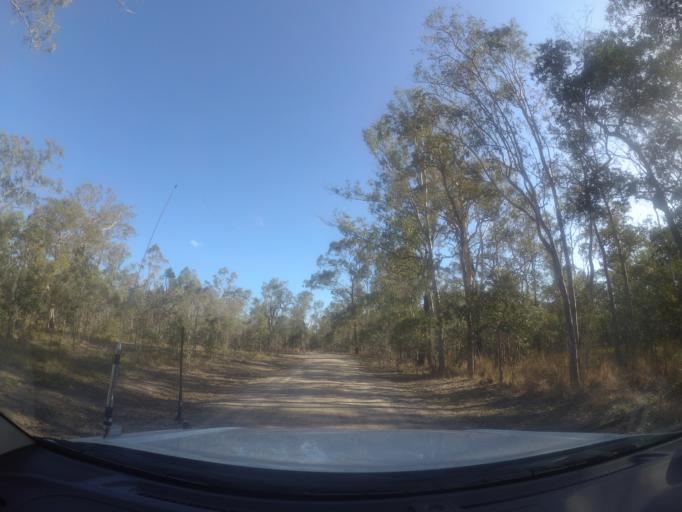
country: AU
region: Queensland
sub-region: Logan
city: Park Ridge South
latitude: -27.7342
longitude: 153.0541
